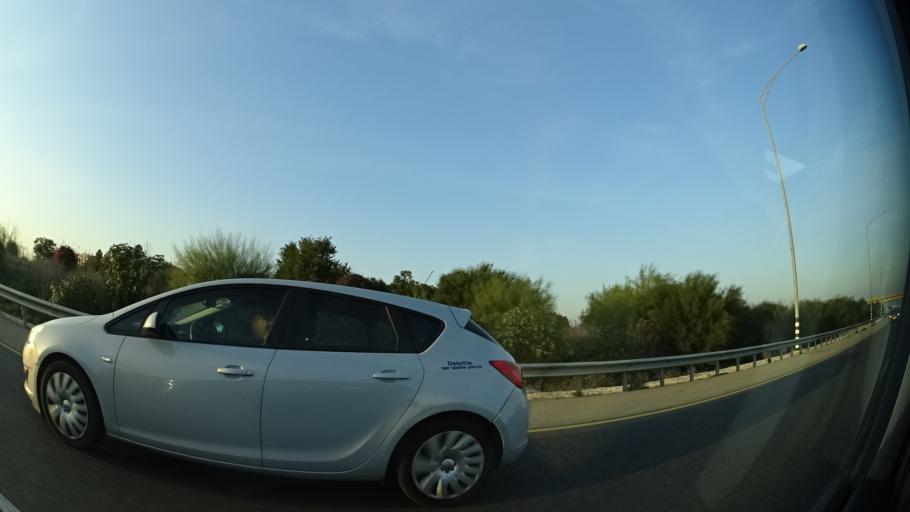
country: IL
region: Central District
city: Kefar Habad
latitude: 31.9919
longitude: 34.8670
